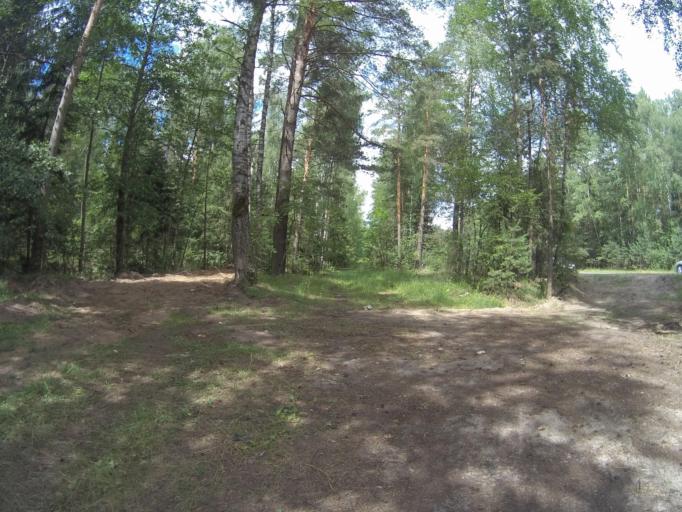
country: RU
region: Vladimir
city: Kommunar
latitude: 56.0561
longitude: 40.5187
